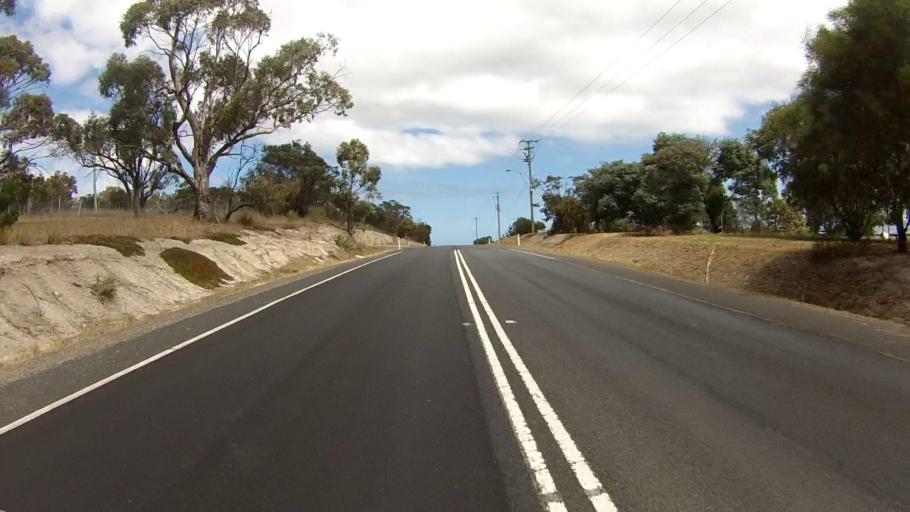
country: AU
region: Tasmania
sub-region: Sorell
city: Sorell
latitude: -42.8167
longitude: 147.6249
